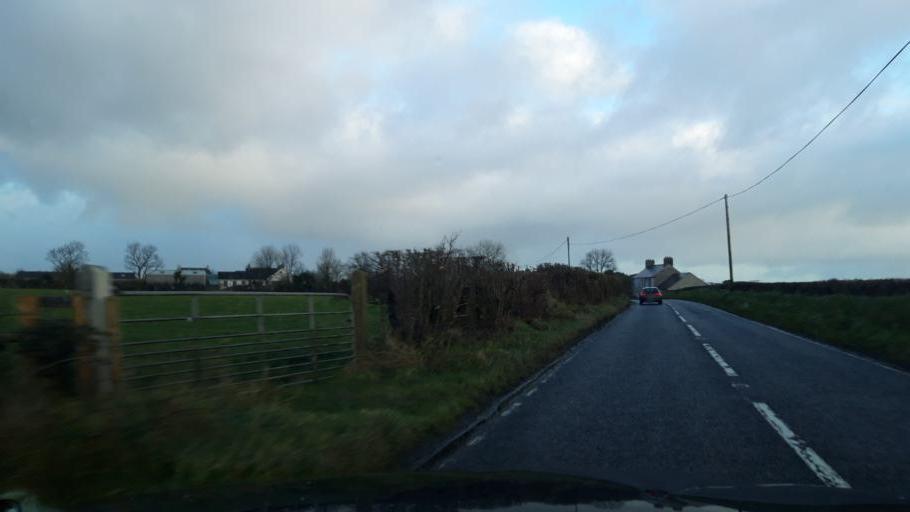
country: GB
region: Northern Ireland
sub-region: Moyle District
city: Ballycastle
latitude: 55.1864
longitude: -6.2833
